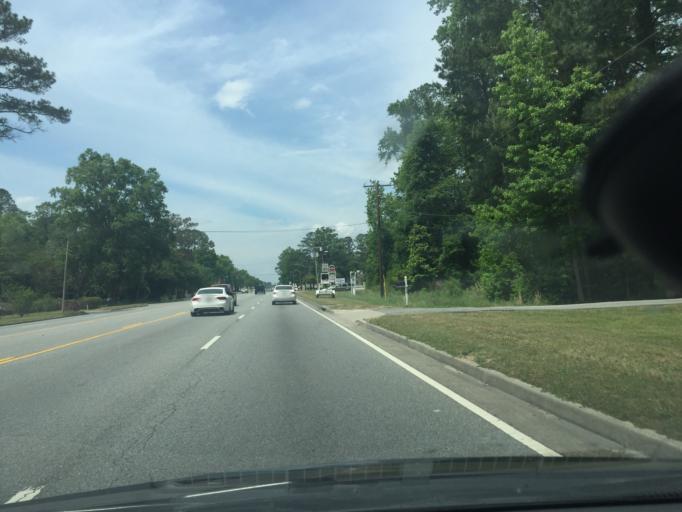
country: US
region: Georgia
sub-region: Chatham County
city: Bloomingdale
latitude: 32.1300
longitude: -81.2916
